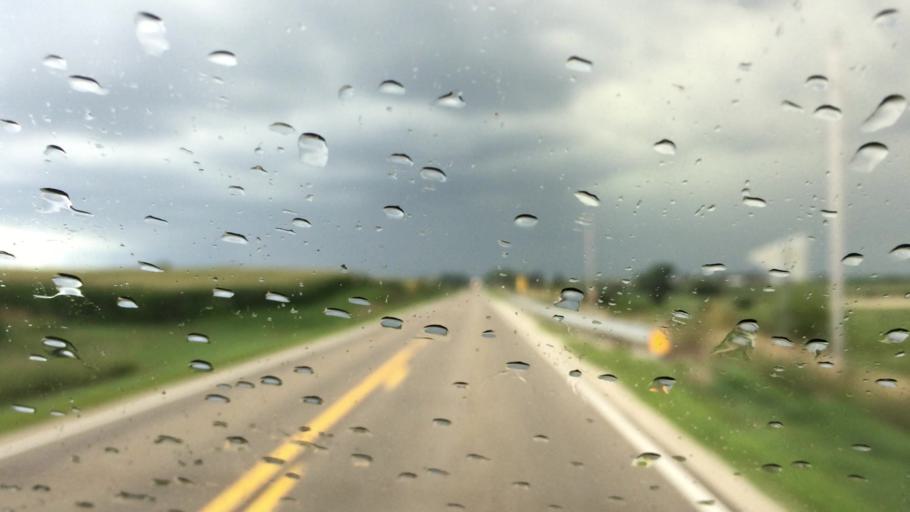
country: US
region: Iowa
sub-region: Henry County
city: Mount Pleasant
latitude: 40.7843
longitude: -91.5280
